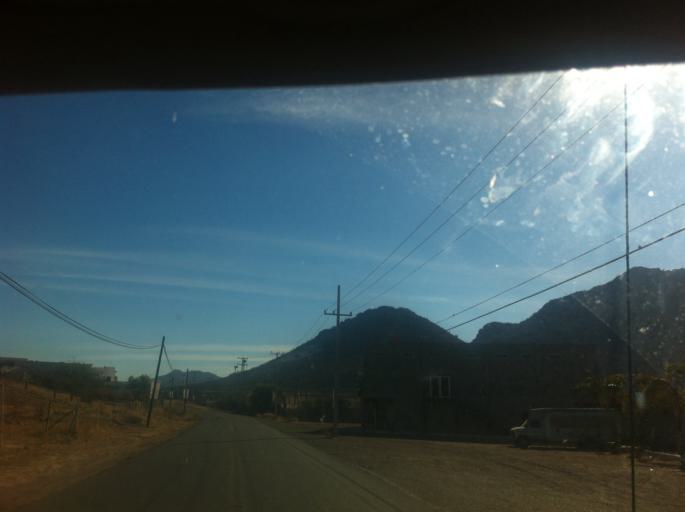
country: MX
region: Sonora
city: Heroica Guaymas
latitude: 27.9277
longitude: -110.9357
